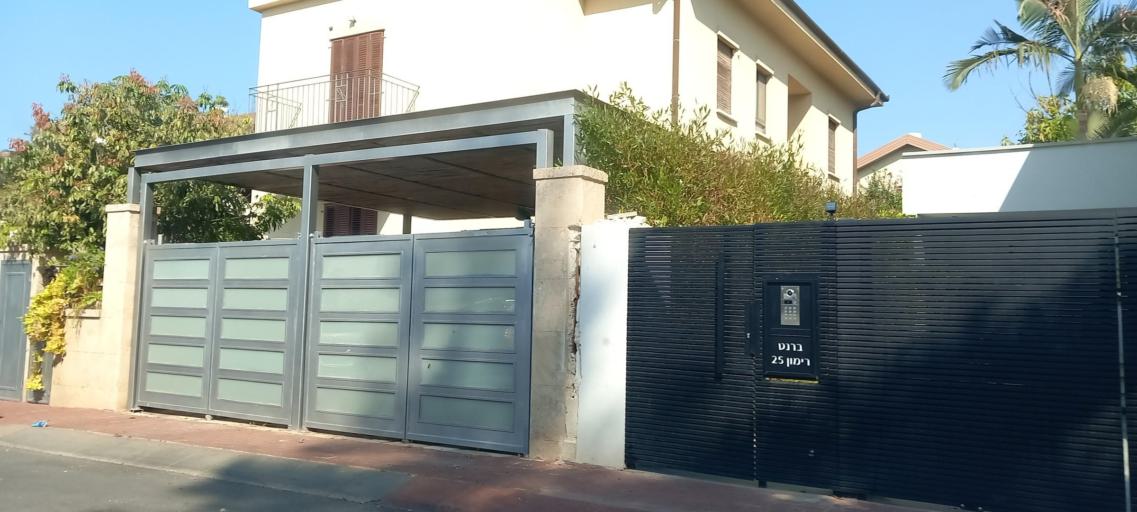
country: IL
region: Tel Aviv
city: Or Yehuda
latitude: 32.0431
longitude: 34.8378
